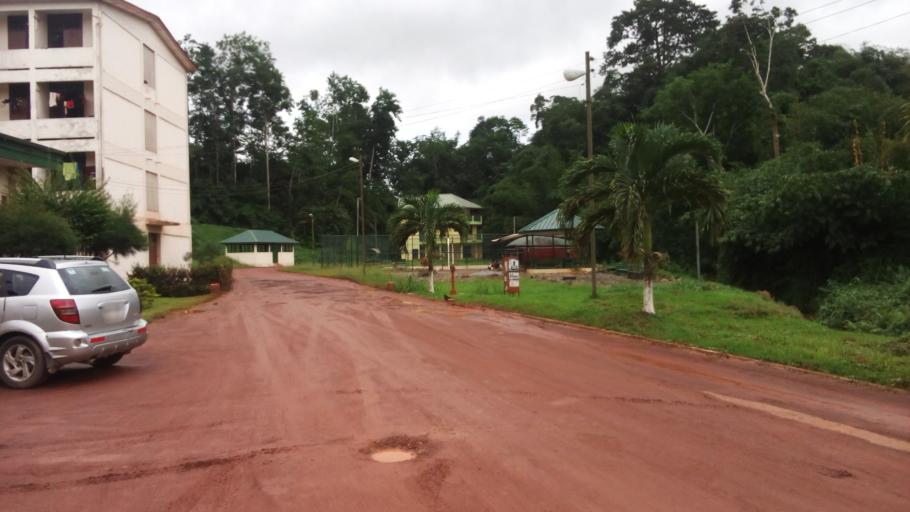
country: GH
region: Western
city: Tarkwa
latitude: 5.2993
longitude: -2.0029
